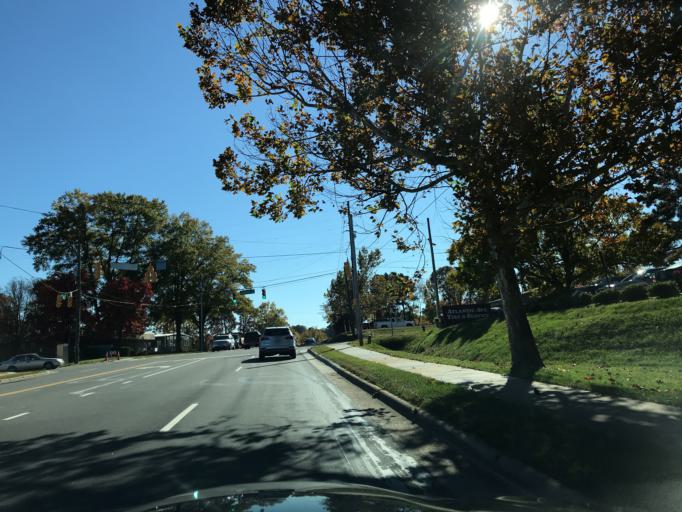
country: US
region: North Carolina
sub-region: Wake County
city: Raleigh
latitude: 35.8406
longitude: -78.6014
